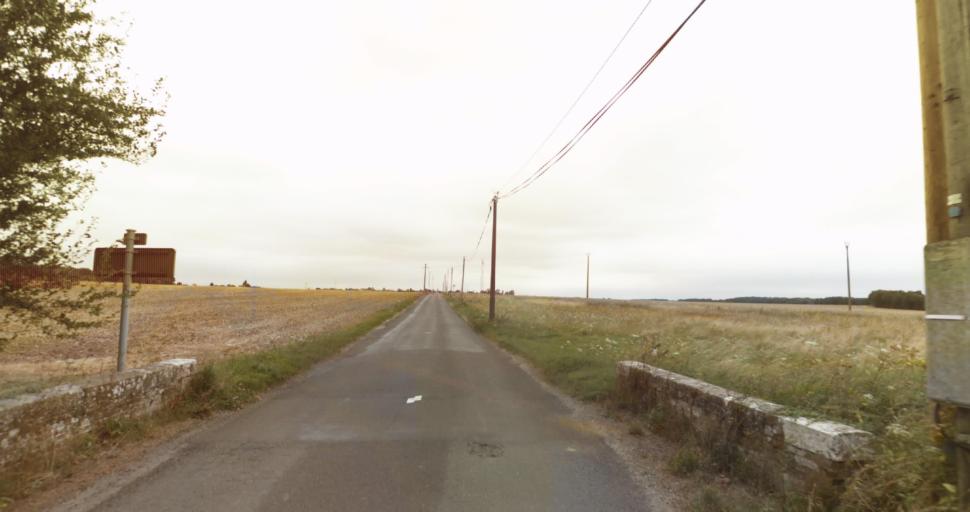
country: FR
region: Haute-Normandie
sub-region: Departement de l'Eure
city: La Couture-Boussey
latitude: 48.8972
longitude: 1.3600
